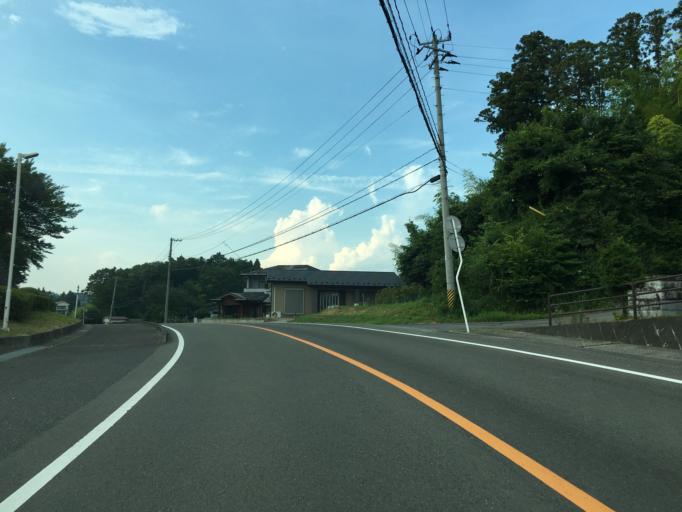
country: JP
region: Fukushima
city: Motomiya
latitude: 37.5265
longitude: 140.4448
